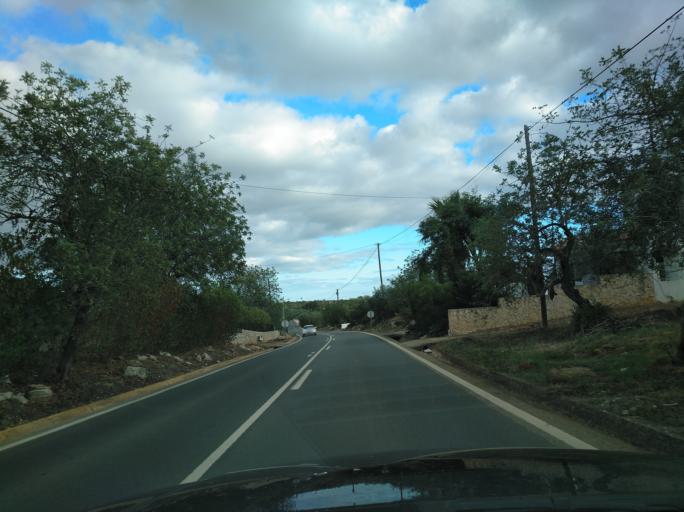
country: PT
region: Faro
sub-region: Tavira
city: Luz
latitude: 37.1393
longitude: -7.7087
